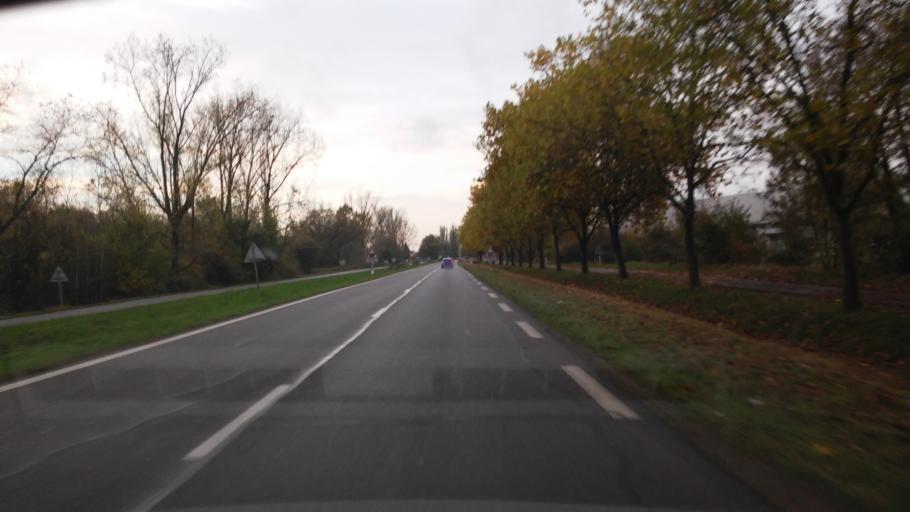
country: FR
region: Lorraine
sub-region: Departement de la Moselle
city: Ennery
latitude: 49.2313
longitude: 6.2095
